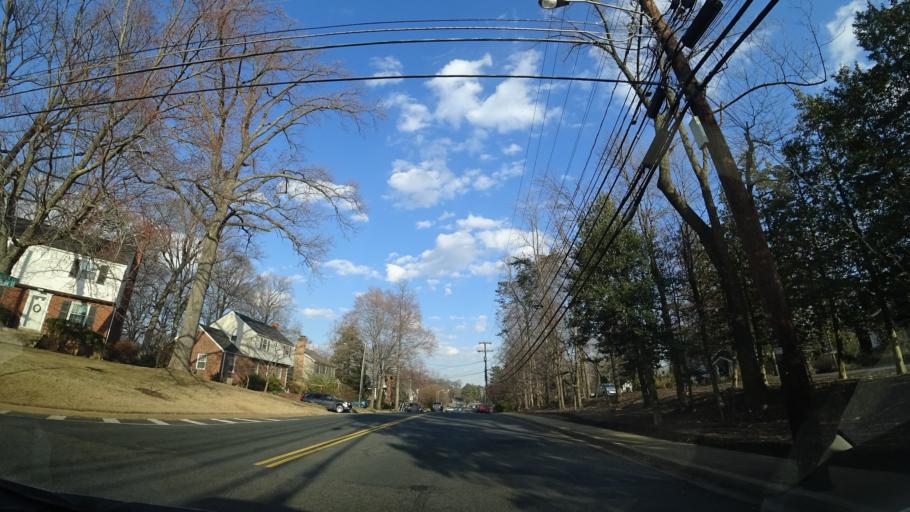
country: US
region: Virginia
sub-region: City of Falls Church
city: Falls Church
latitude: 38.8903
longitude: -77.1692
